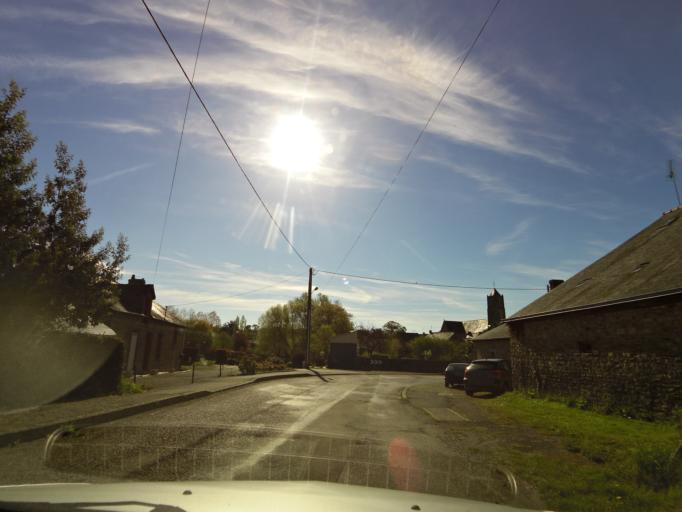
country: FR
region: Brittany
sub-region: Departement d'Ille-et-Vilaine
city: Tresboeuf
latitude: 47.8707
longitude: -1.6000
